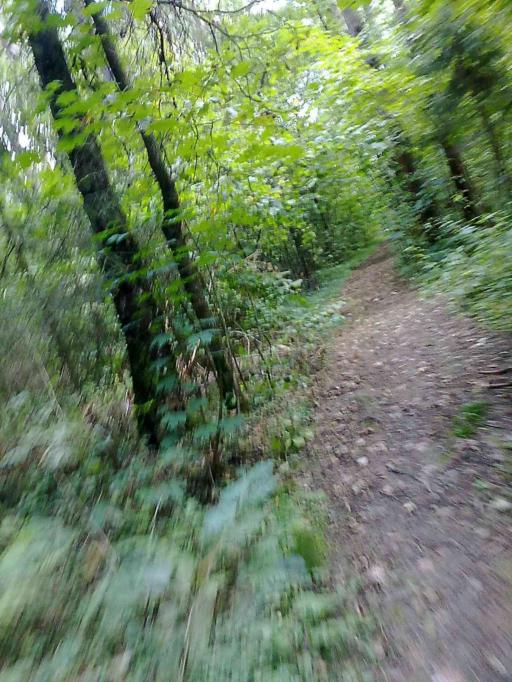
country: RU
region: Moscow
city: Tolstopal'tsevo
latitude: 55.6233
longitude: 37.2536
